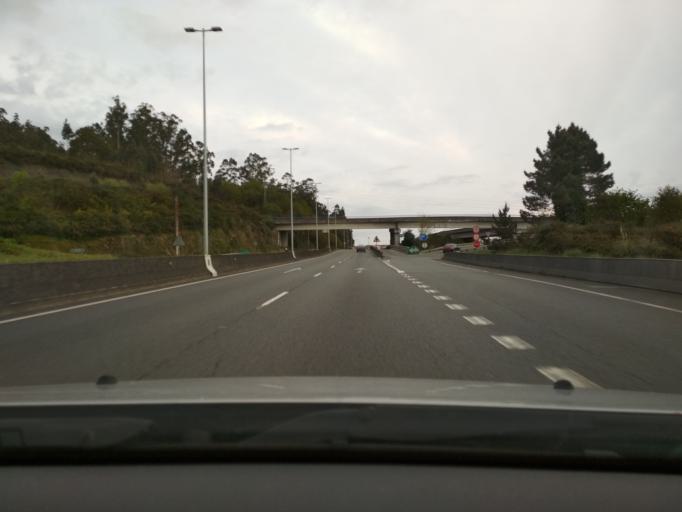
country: ES
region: Galicia
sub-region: Provincia da Coruna
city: Santiago de Compostela
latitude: 42.8544
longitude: -8.5713
